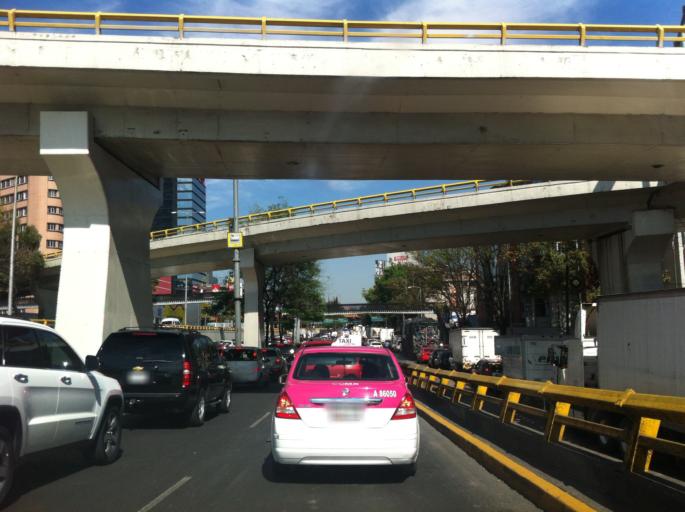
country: MX
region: Mexico City
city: Cuauhtemoc
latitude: 19.4334
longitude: -99.1714
